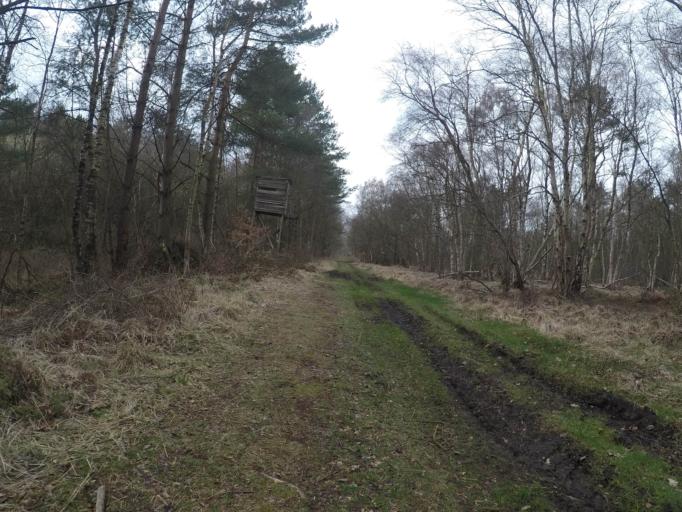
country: DE
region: Lower Saxony
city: Elmlohe
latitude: 53.6228
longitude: 8.6822
